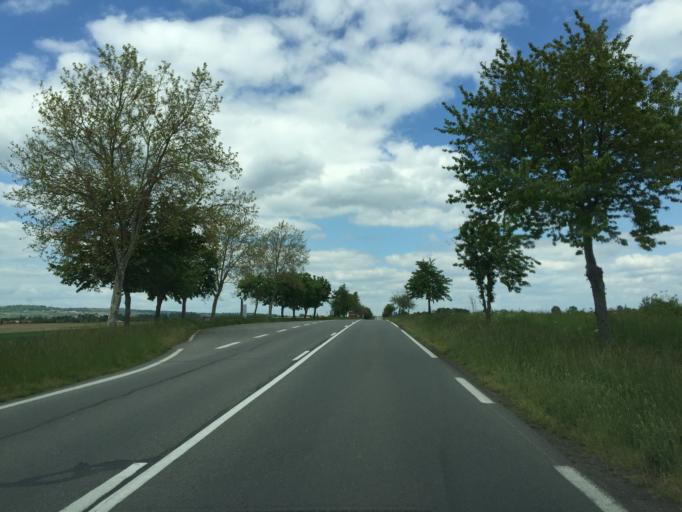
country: FR
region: Auvergne
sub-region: Departement du Puy-de-Dome
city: Aigueperse
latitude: 45.9677
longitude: 3.1779
